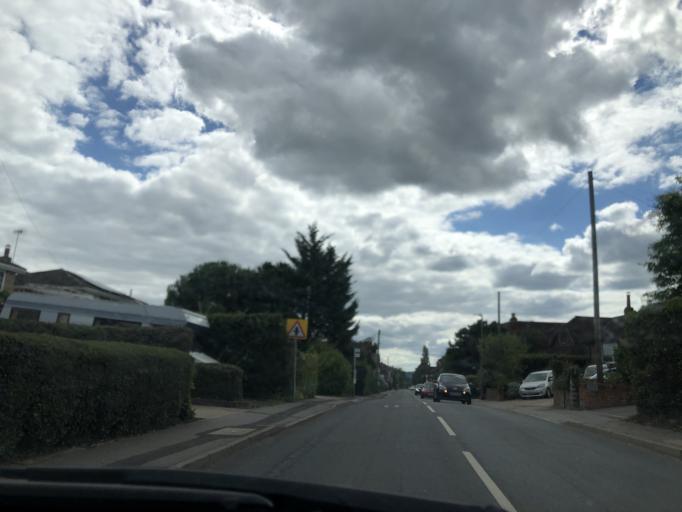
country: GB
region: England
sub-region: Kent
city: Edenbridge
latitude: 51.2134
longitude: 0.0597
